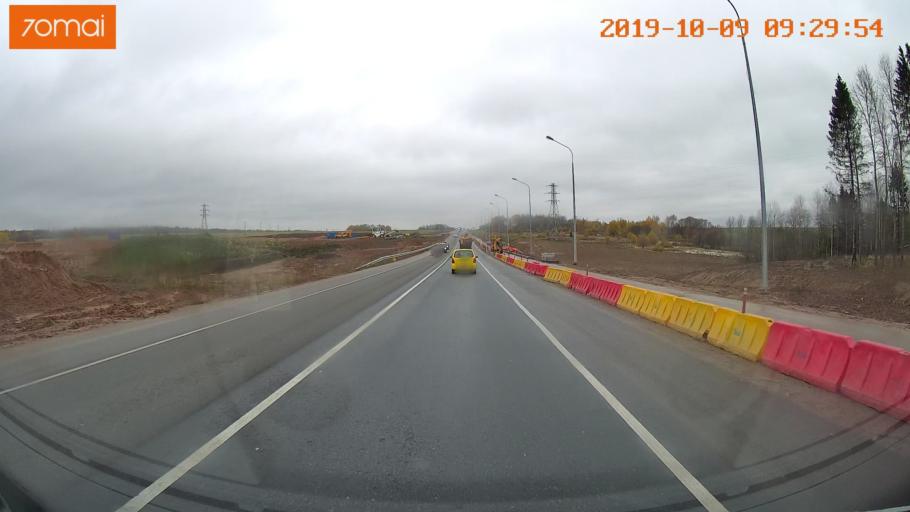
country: RU
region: Vologda
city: Vologda
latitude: 59.1355
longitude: 39.9540
